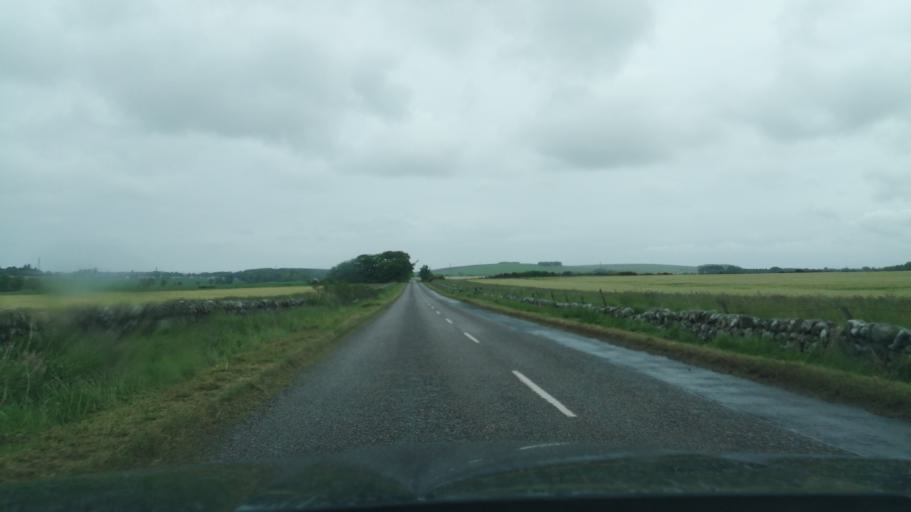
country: GB
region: Scotland
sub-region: Aberdeenshire
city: Portsoy
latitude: 57.6600
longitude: -2.6979
